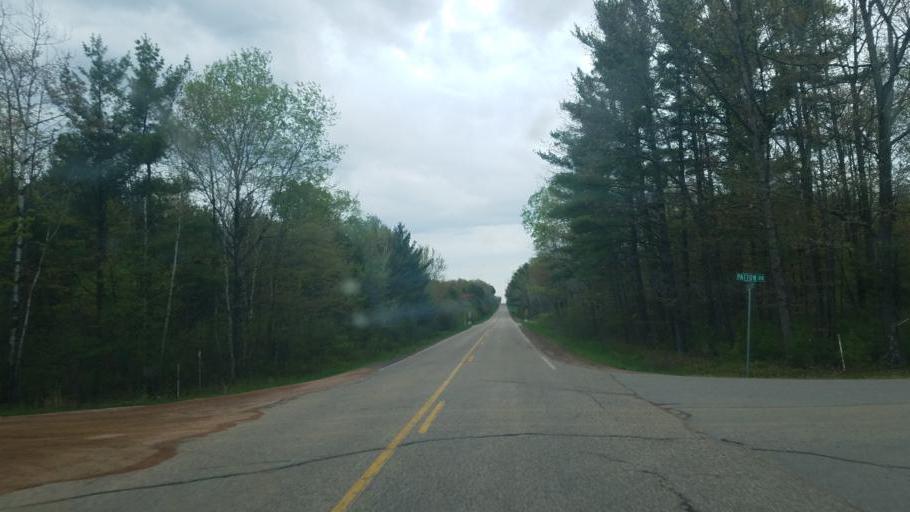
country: US
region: Wisconsin
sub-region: Wood County
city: Marshfield
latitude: 44.5412
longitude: -90.2999
